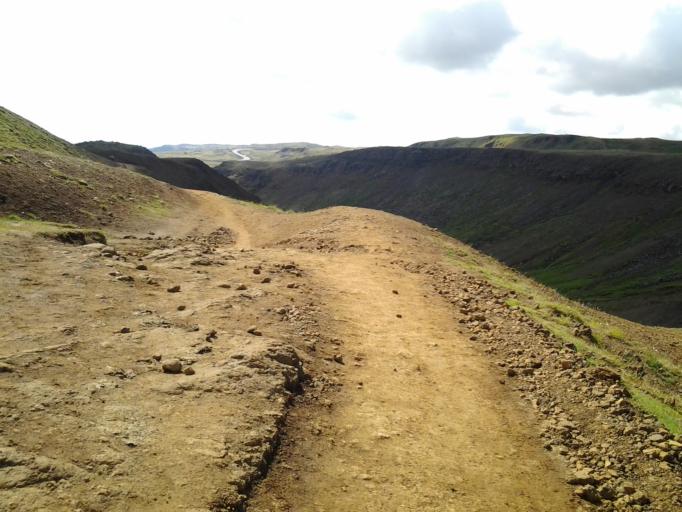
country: IS
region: South
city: Hveragerdi
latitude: 64.0360
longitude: -21.2187
